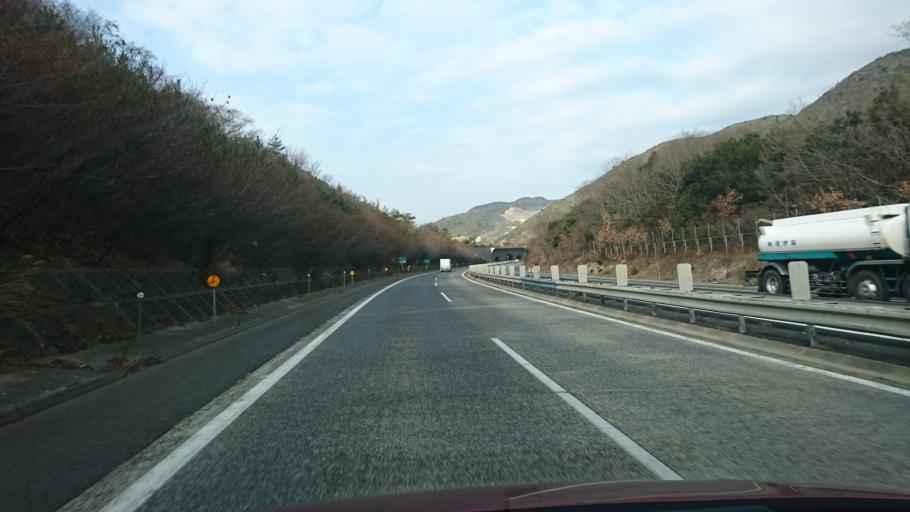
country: JP
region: Hyogo
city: Kariya
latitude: 34.7769
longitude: 134.3497
